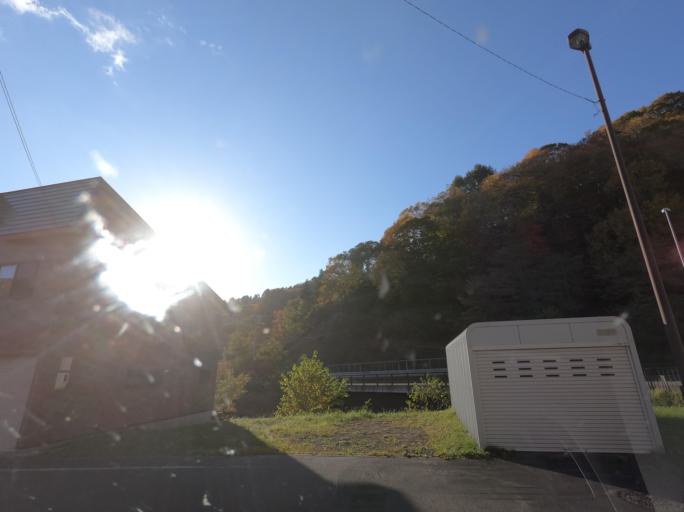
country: JP
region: Hokkaido
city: Iwamizawa
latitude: 43.0591
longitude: 141.9764
